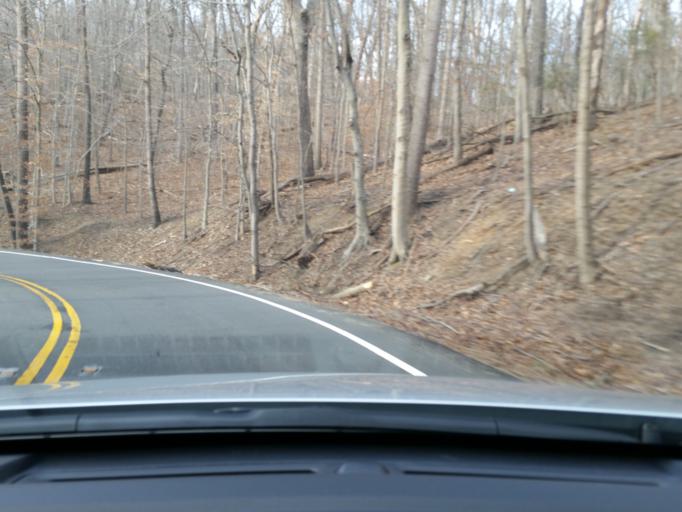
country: US
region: Virginia
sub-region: Fairfax County
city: Great Falls
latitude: 38.9783
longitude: -77.2486
